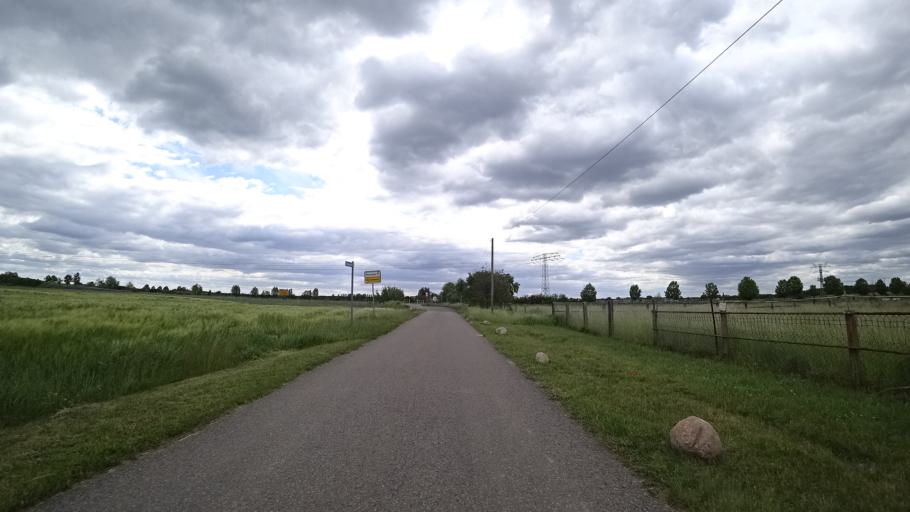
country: DE
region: Brandenburg
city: Trebbin
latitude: 52.1870
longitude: 13.2451
